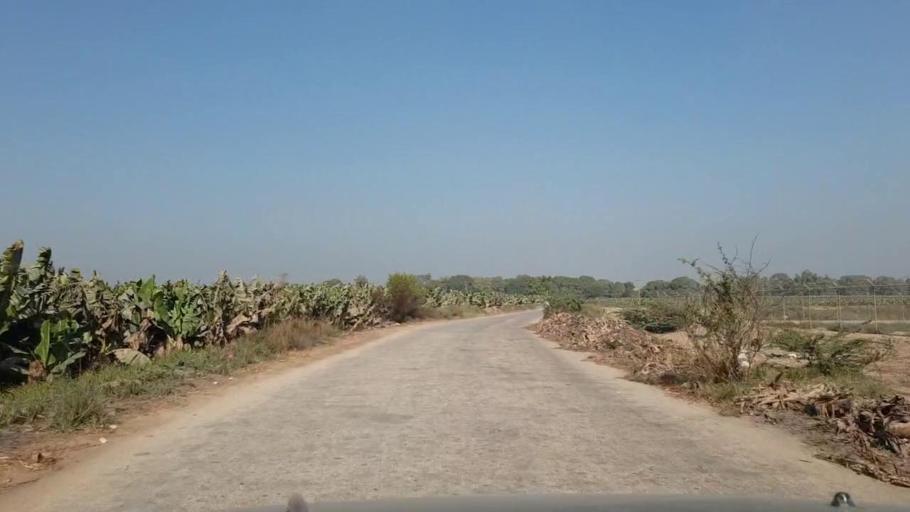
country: PK
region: Sindh
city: Matiari
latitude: 25.6159
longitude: 68.5942
